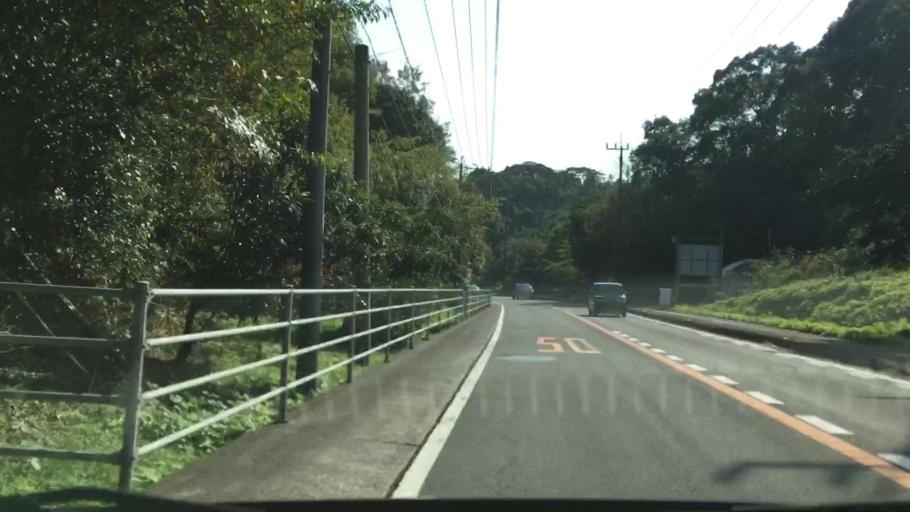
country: JP
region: Nagasaki
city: Togitsu
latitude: 32.9583
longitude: 129.7825
